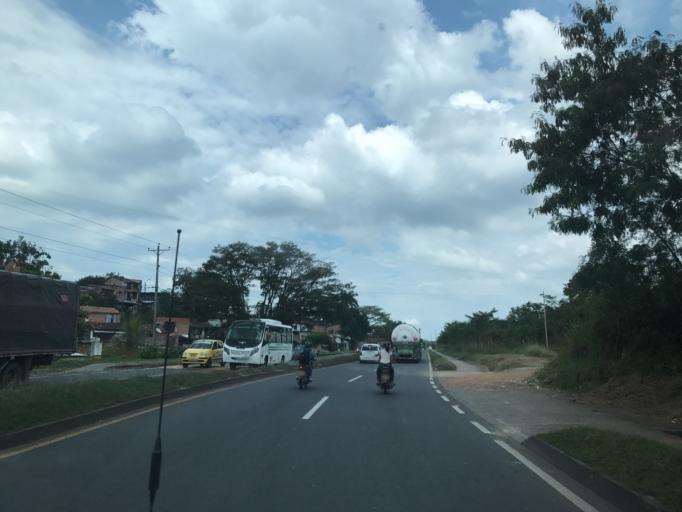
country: CO
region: Valle del Cauca
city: Cartago
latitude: 4.7602
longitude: -75.8992
